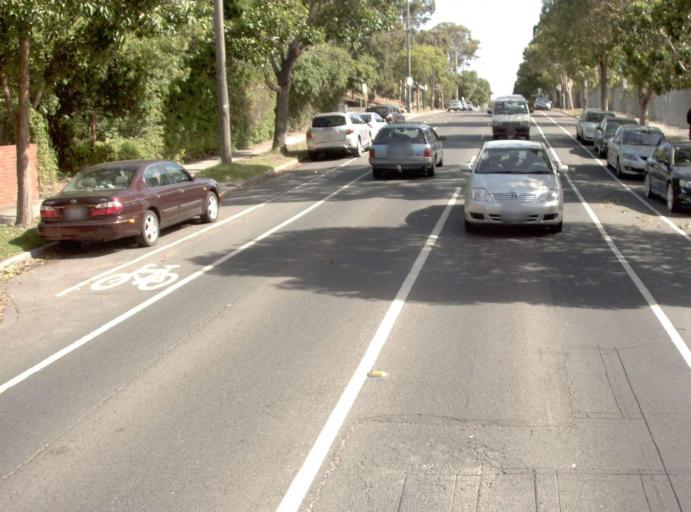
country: AU
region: Victoria
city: Glenferrie
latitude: -37.8422
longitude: 145.0456
